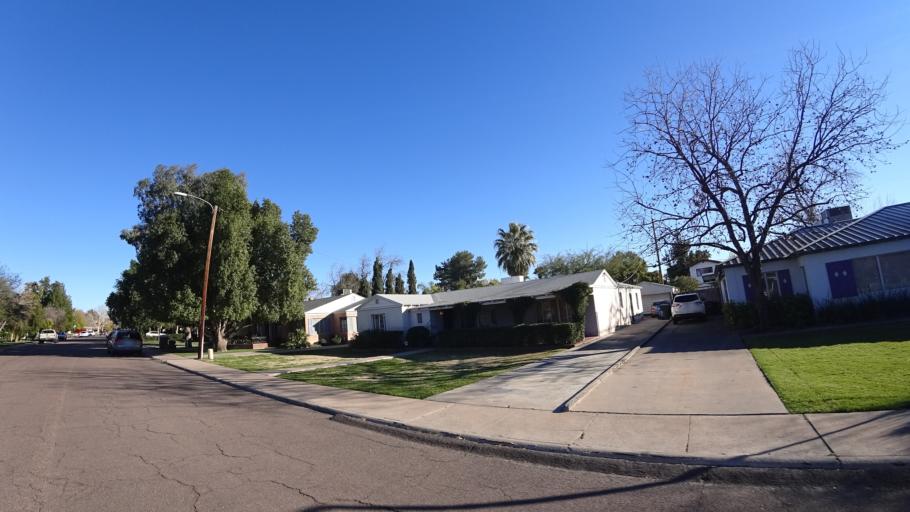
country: US
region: Arizona
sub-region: Maricopa County
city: Phoenix
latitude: 33.5120
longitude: -112.0692
